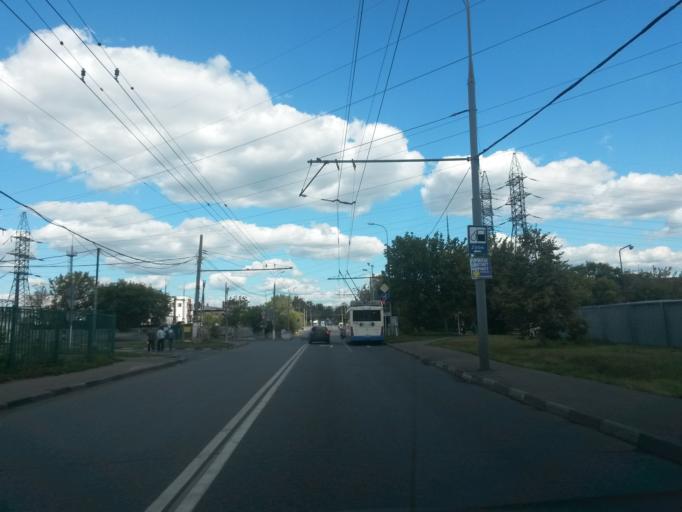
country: RU
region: Moscow
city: Mar'ino
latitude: 55.6562
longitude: 37.7264
